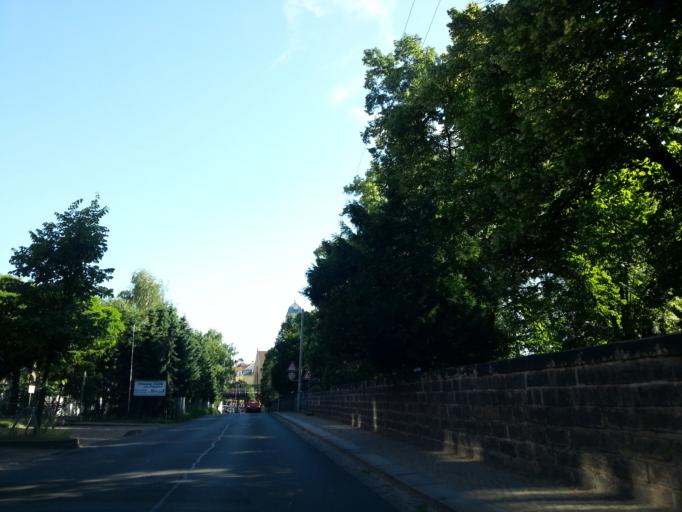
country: DE
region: Saxony
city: Dresden
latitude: 51.0857
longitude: 13.7214
